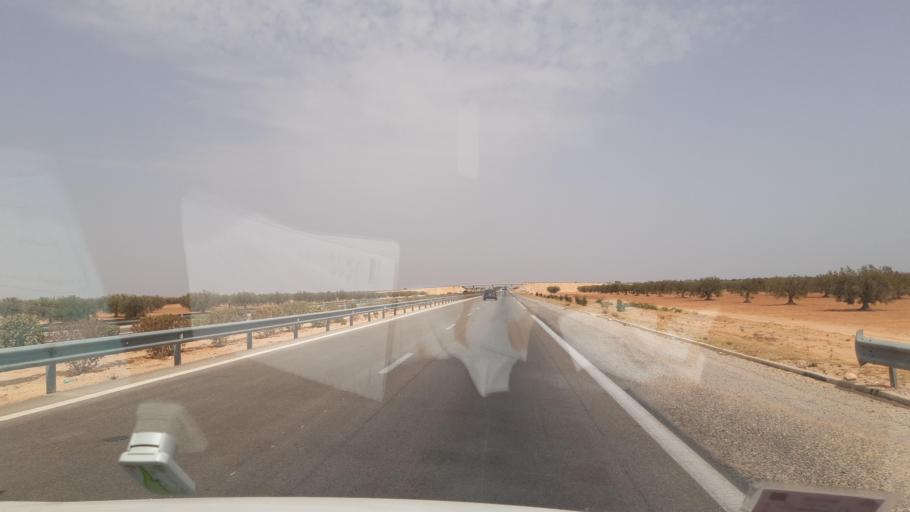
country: TN
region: Safaqis
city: Bi'r `Ali Bin Khalifah
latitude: 34.5724
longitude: 10.3842
